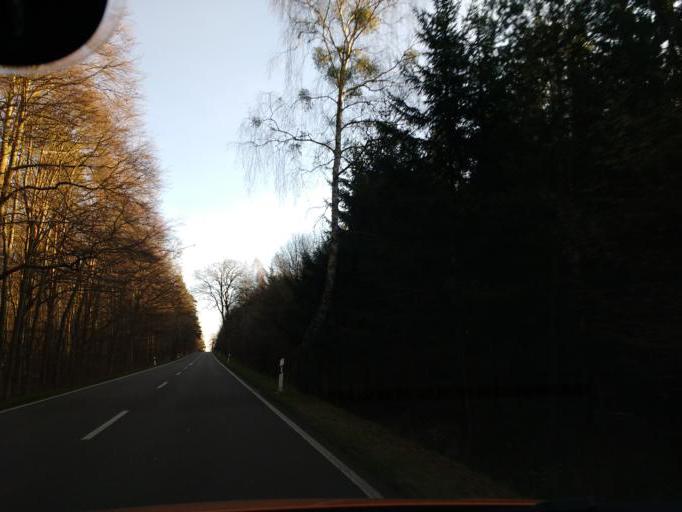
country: DE
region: Brandenburg
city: Protzel
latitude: 52.6448
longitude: 13.9436
